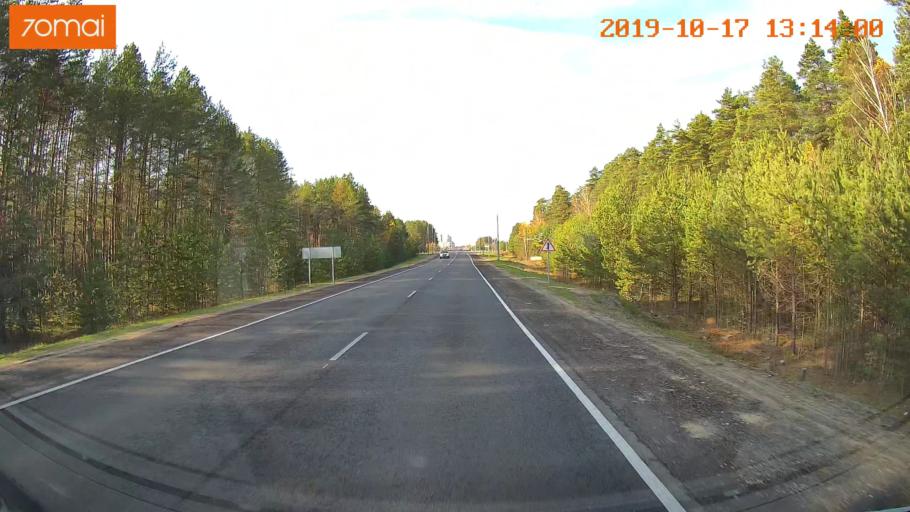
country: RU
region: Rjazan
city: Gus'-Zheleznyy
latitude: 55.0495
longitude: 41.1793
